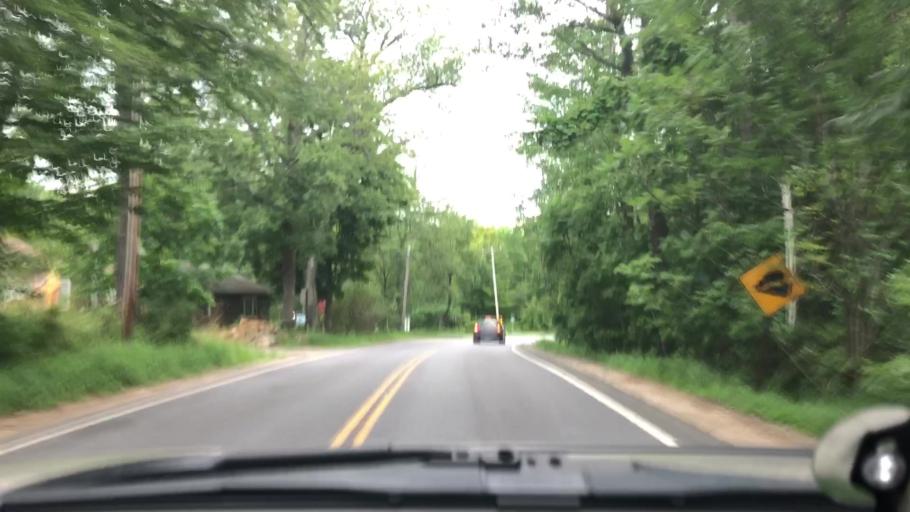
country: US
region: New York
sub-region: Saratoga County
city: Corinth
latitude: 43.2064
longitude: -73.7731
